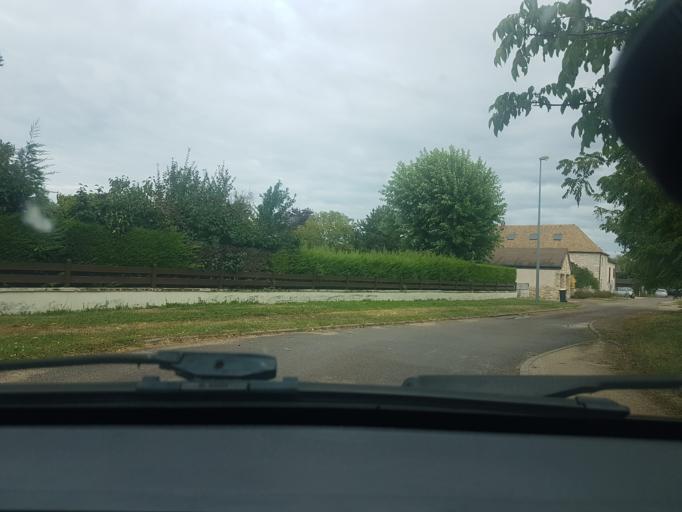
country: FR
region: Bourgogne
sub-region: Departement de Saone-et-Loire
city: Fontaines
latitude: 46.8641
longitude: 4.7598
